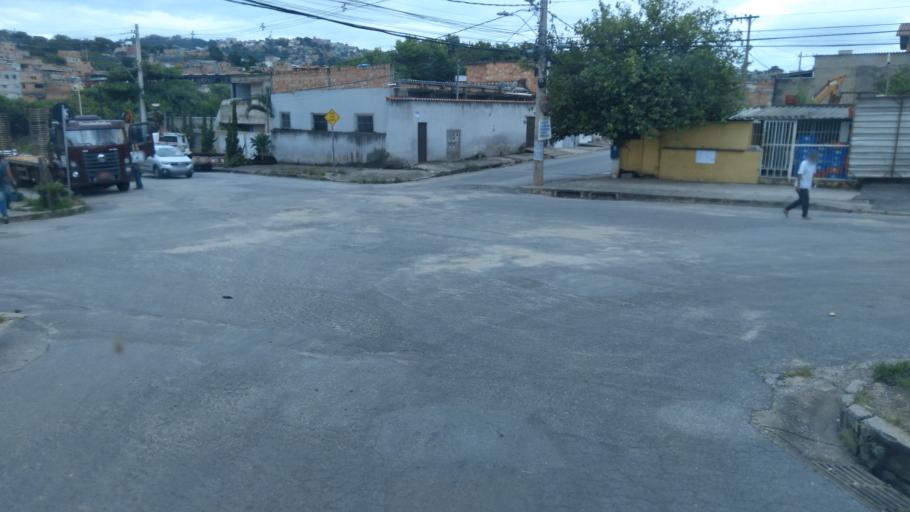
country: BR
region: Minas Gerais
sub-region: Belo Horizonte
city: Belo Horizonte
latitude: -19.8454
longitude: -43.9082
